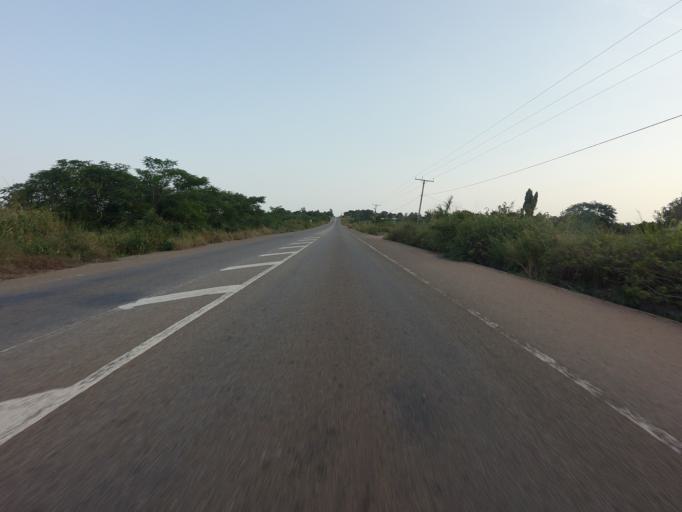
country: GH
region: Volta
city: Anloga
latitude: 6.0575
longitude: 0.6045
